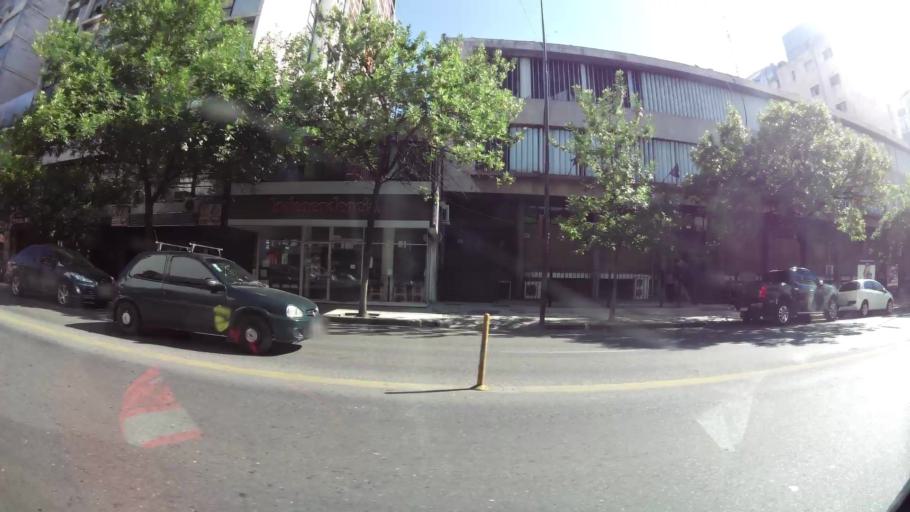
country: AR
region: Cordoba
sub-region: Departamento de Capital
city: Cordoba
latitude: -31.4125
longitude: -64.1862
